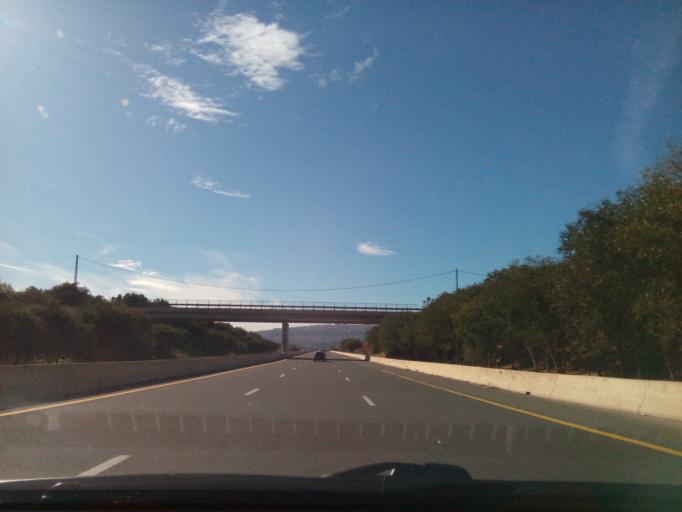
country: DZ
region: Tlemcen
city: Chetouane
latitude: 34.9522
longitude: -1.3018
